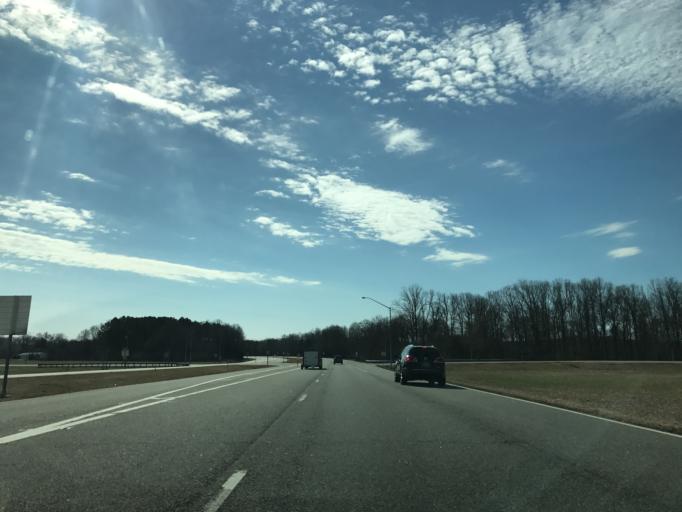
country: US
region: Maryland
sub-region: Queen Anne's County
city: Kingstown
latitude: 39.2427
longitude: -75.8737
